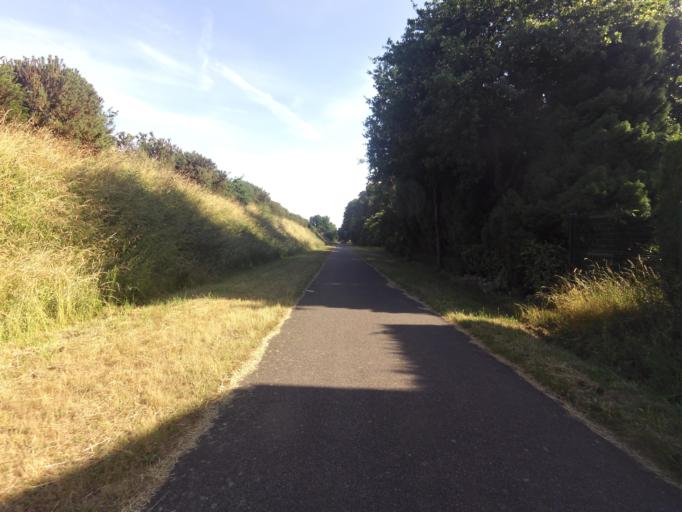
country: FR
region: Brittany
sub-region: Departement du Morbihan
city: Guillac
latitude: 47.8628
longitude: -2.4389
